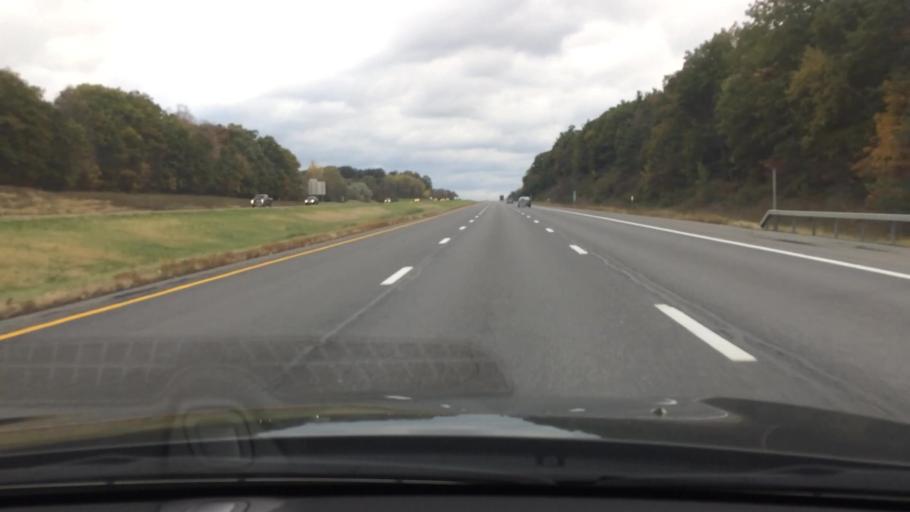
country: US
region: New York
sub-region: Rensselaer County
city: East Greenbush
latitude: 42.6141
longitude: -73.6887
